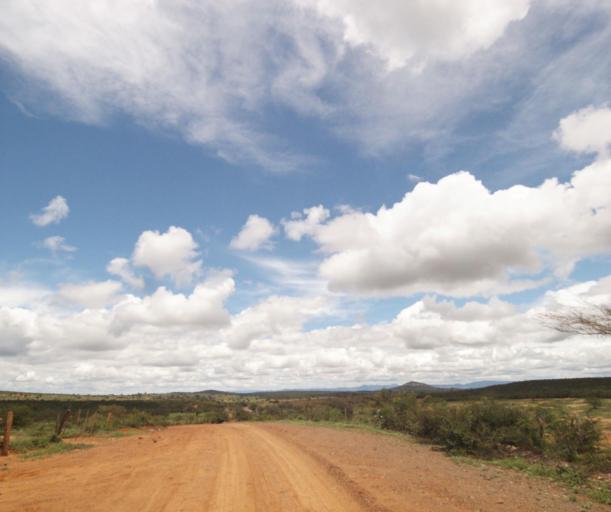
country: BR
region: Bahia
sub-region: Tanhacu
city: Tanhacu
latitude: -14.1852
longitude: -41.0867
